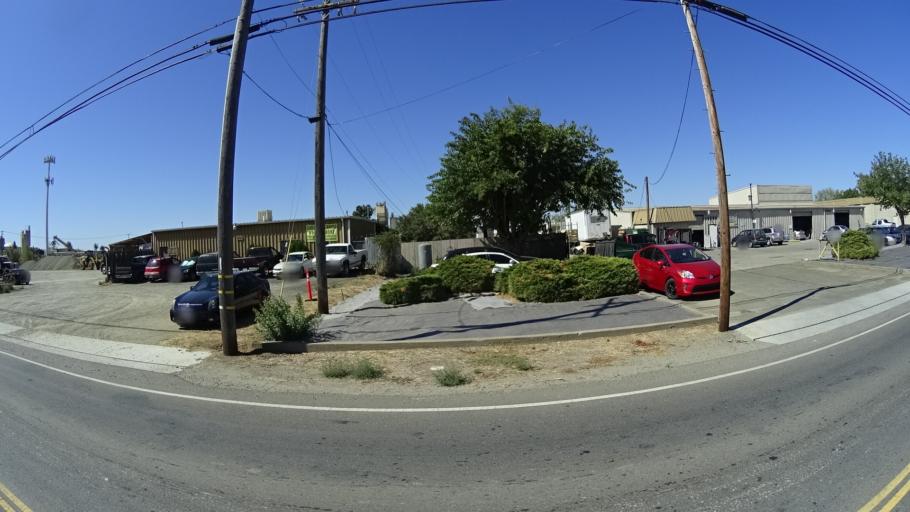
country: US
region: California
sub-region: Sacramento County
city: Elk Grove
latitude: 38.3887
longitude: -121.3529
